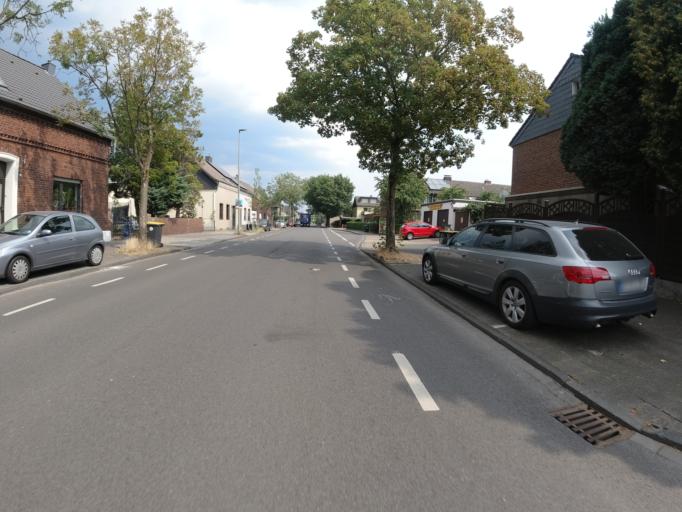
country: DE
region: North Rhine-Westphalia
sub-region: Regierungsbezirk Dusseldorf
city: Moers
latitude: 51.3921
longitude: 6.6474
